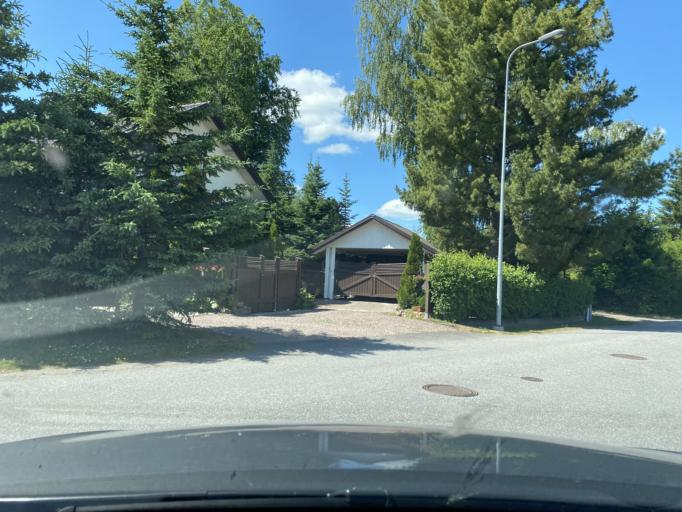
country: FI
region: Satakunta
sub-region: Rauma
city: Eura
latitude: 61.1136
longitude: 22.1461
